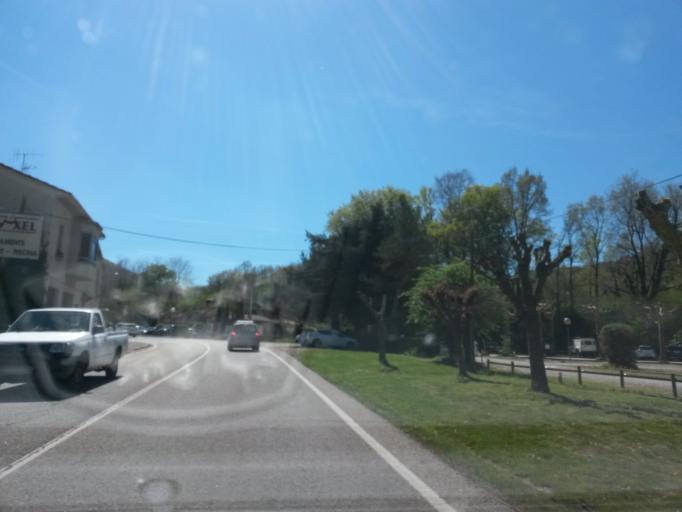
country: ES
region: Catalonia
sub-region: Provincia de Girona
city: Sant Cristofol de les Fonts
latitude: 42.1489
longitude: 2.5303
